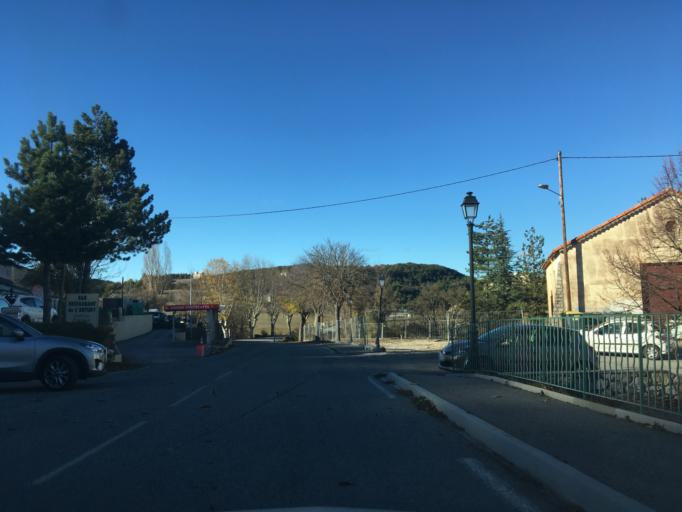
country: FR
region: Provence-Alpes-Cote d'Azur
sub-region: Departement du Var
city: Bargemon
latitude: 43.7106
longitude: 6.5070
